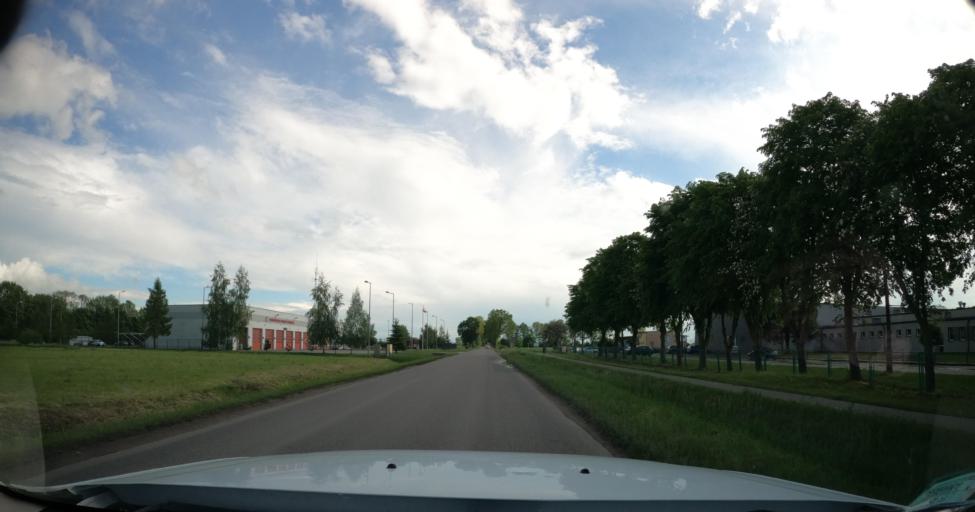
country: PL
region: Pomeranian Voivodeship
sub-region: Powiat nowodworski
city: Nowy Dwor Gdanski
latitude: 54.2067
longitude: 19.1366
